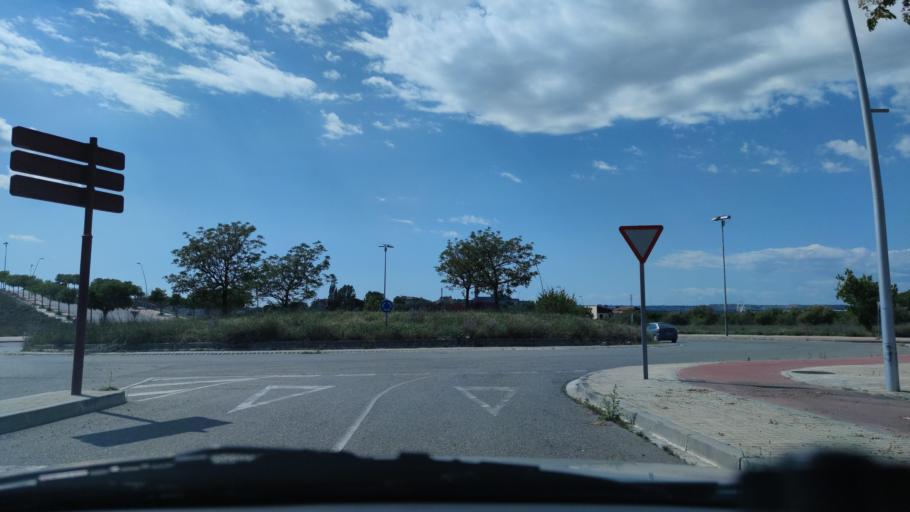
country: ES
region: Catalonia
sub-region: Provincia de Lleida
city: Lleida
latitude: 41.6072
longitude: 0.6535
